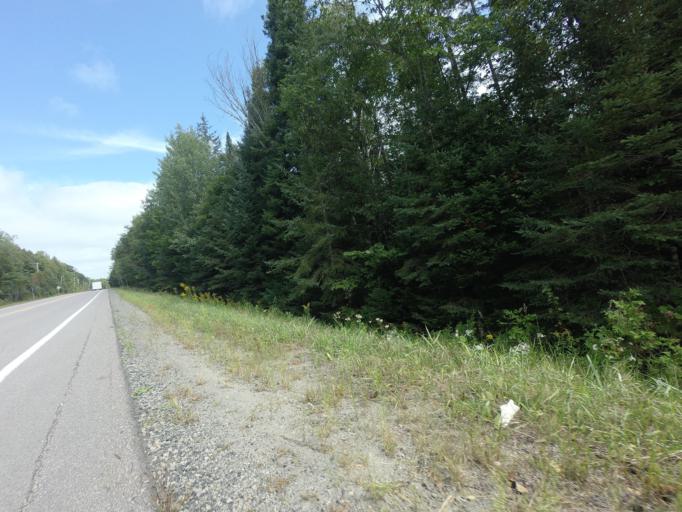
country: CA
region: Ontario
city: Bancroft
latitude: 44.9132
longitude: -78.3577
